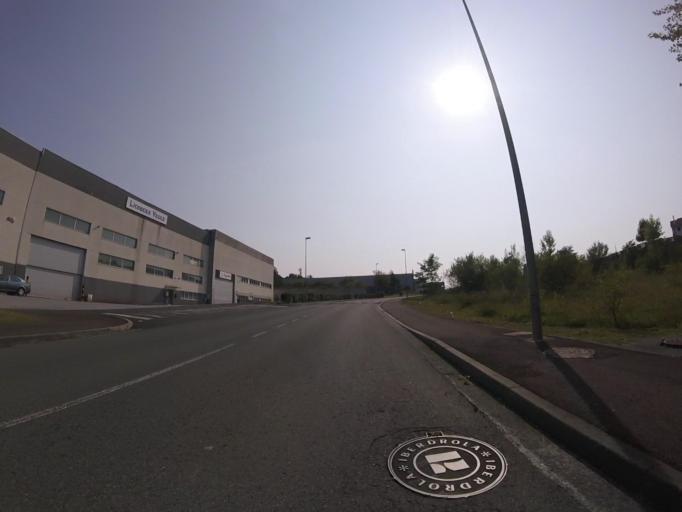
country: ES
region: Basque Country
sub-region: Provincia de Guipuzcoa
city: Errenteria
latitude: 43.2958
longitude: -1.8982
